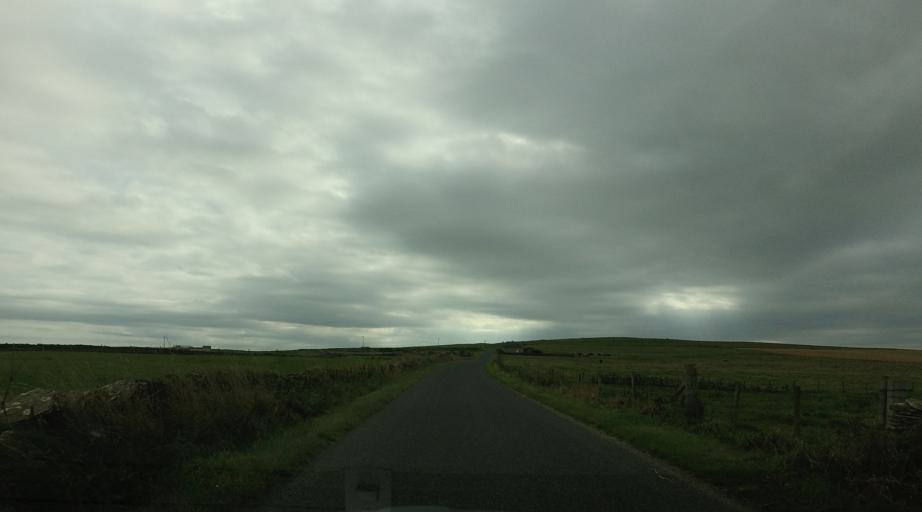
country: GB
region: Scotland
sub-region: Orkney Islands
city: Stromness
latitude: 59.0326
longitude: -3.3136
